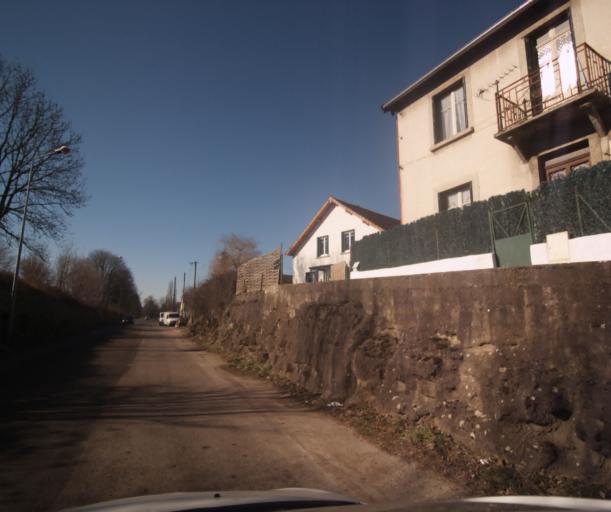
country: FR
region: Franche-Comte
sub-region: Departement du Doubs
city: Besancon
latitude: 47.2372
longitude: 5.9922
